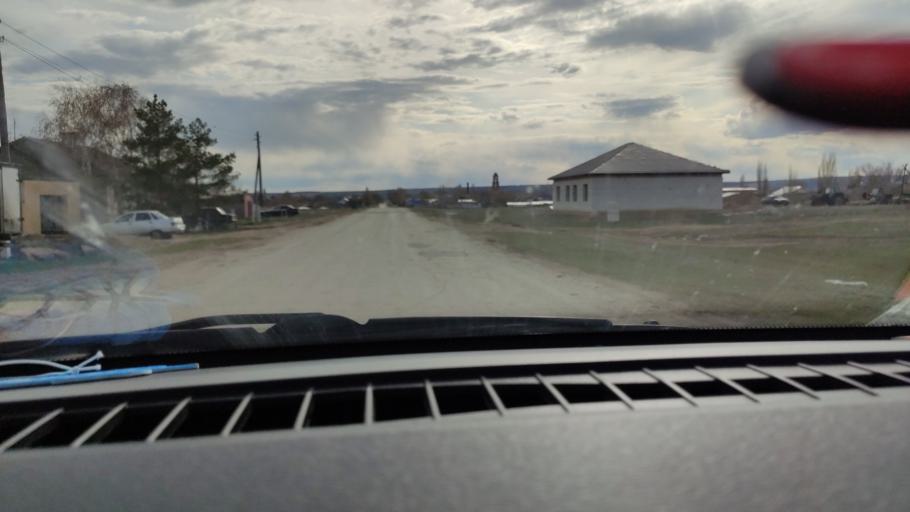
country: RU
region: Saratov
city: Rovnoye
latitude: 50.9286
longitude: 46.0843
